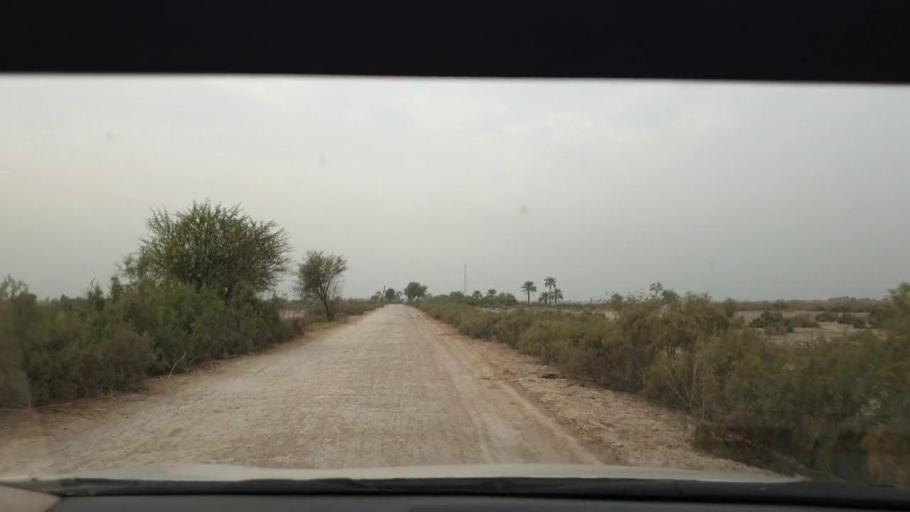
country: PK
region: Sindh
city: Sinjhoro
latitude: 25.9283
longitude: 68.7540
